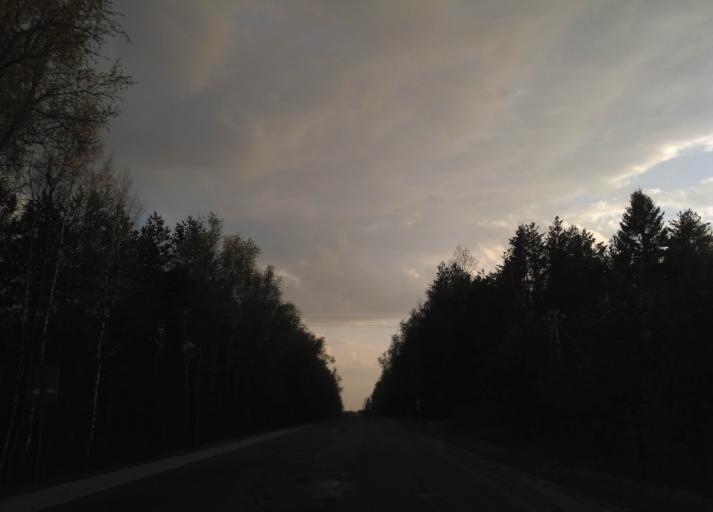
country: BY
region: Minsk
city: Loshnitsa
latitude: 54.4167
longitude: 28.6363
